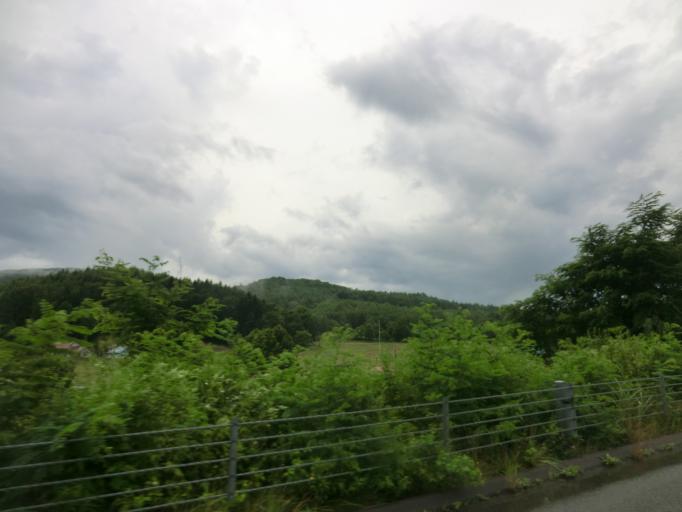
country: JP
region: Hokkaido
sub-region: Asahikawa-shi
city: Asahikawa
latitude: 43.9284
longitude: 142.4675
